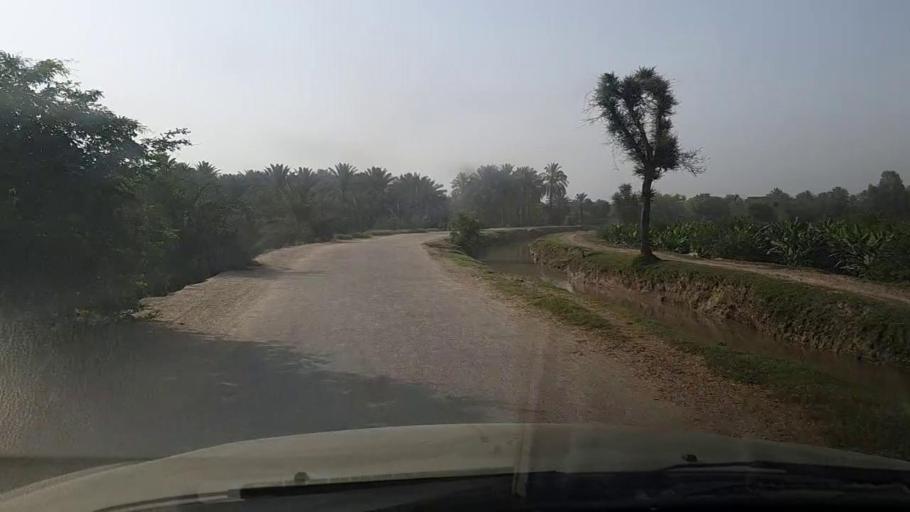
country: PK
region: Sindh
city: Pir jo Goth
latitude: 27.5588
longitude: 68.5462
